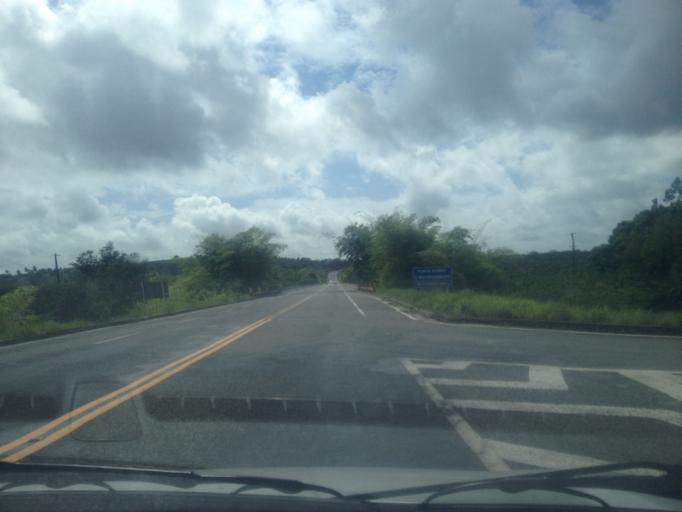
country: BR
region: Bahia
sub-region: Conde
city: Conde
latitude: -12.0634
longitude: -37.7448
